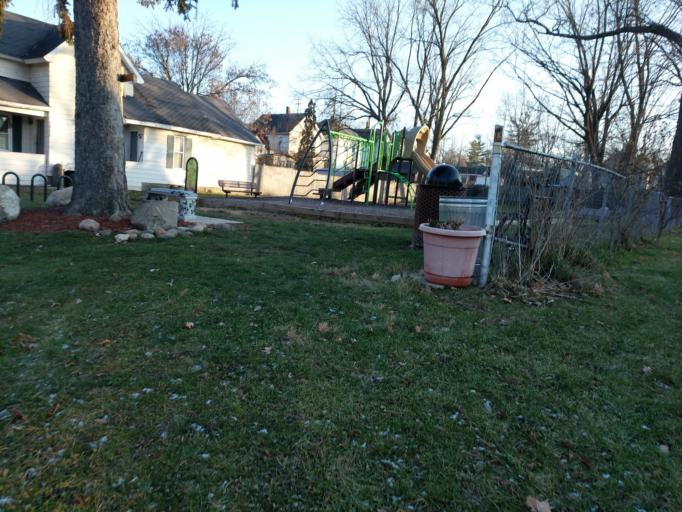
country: US
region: Michigan
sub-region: Ingham County
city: Lansing
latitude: 42.7310
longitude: -84.5358
